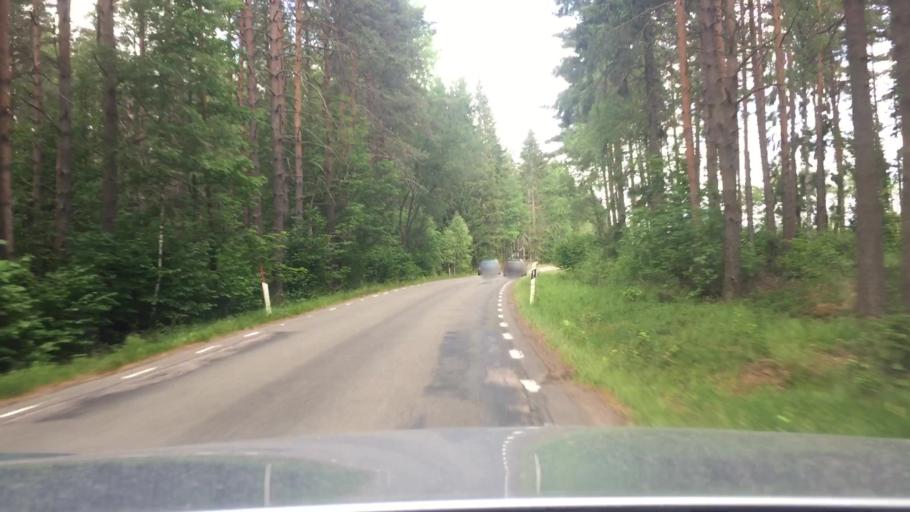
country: SE
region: Vaestra Goetaland
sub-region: Tidaholms Kommun
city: Tidaholm
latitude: 58.2040
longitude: 13.9805
